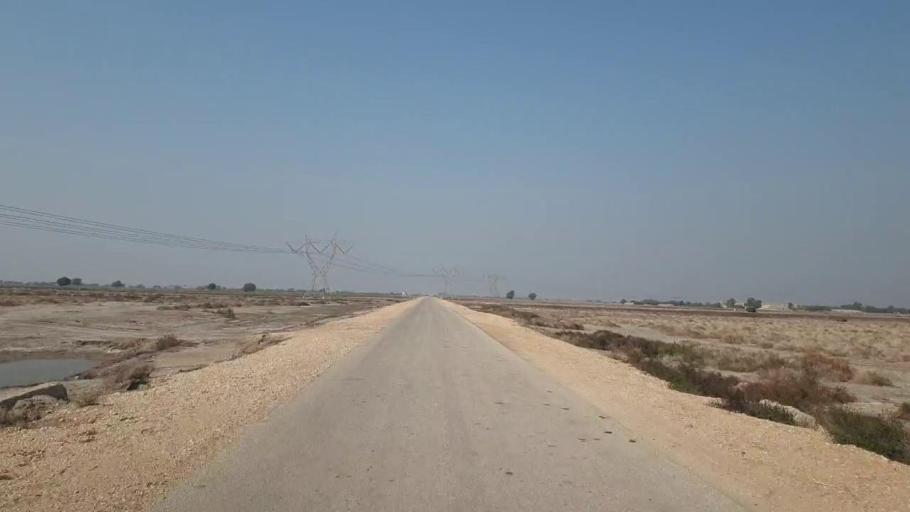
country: PK
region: Sindh
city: Sehwan
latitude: 26.4271
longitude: 67.7725
